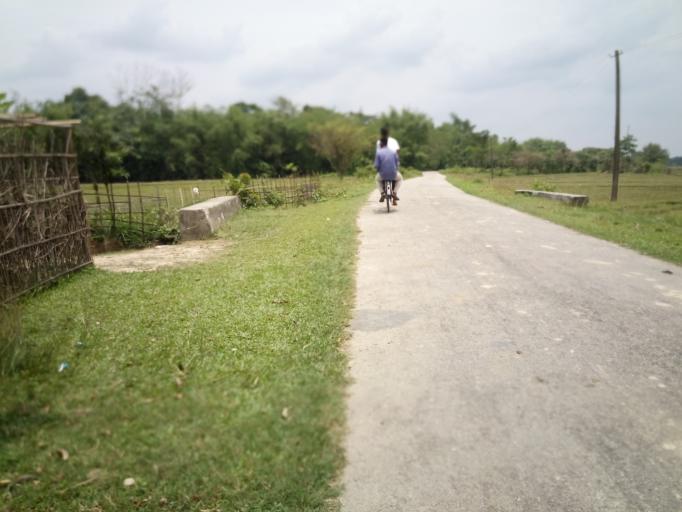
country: IN
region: Assam
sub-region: Udalguri
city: Udalguri
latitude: 26.6950
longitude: 92.0773
